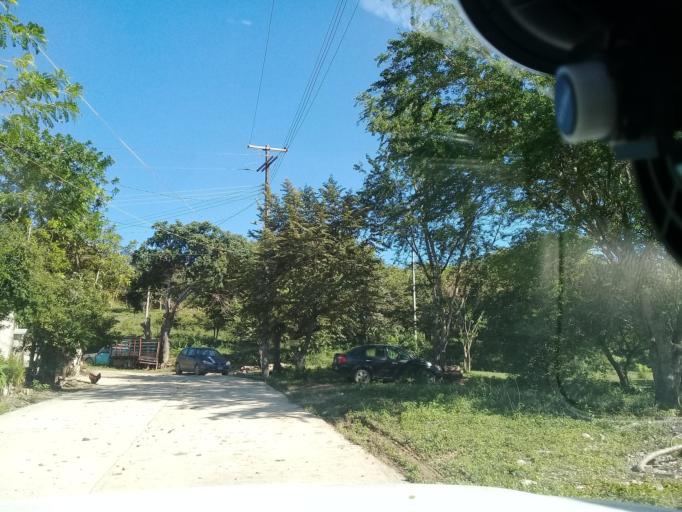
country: MX
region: Hidalgo
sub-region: Huejutla de Reyes
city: Huejutla de Reyes
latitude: 21.1607
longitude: -98.4106
